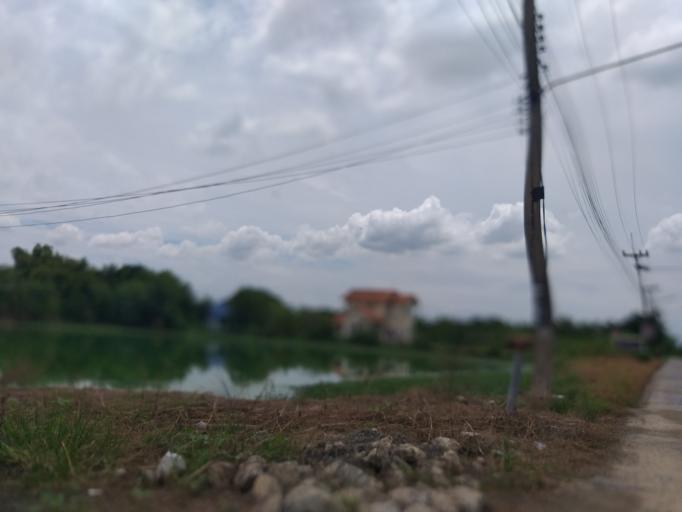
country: TH
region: Pathum Thani
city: Ban Lam Luk Ka
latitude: 13.9728
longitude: 100.8542
